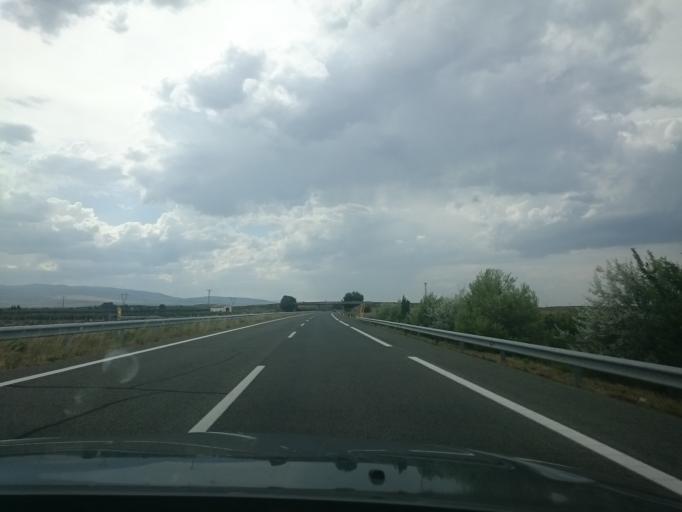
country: ES
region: Navarre
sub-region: Provincia de Navarra
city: Corella
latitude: 42.1527
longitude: -1.8038
